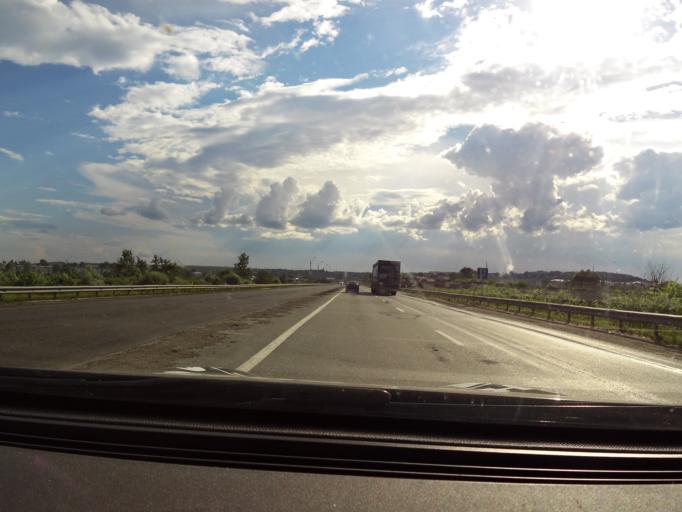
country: RU
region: Vladimir
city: Gorokhovets
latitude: 56.2034
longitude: 42.7194
